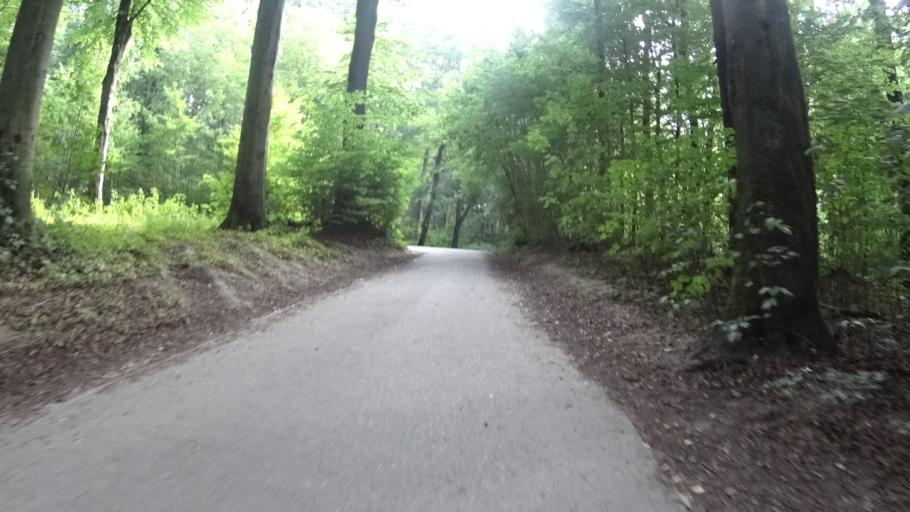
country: DE
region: North Rhine-Westphalia
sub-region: Regierungsbezirk Arnsberg
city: Dortmund
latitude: 51.4861
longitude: 7.4548
